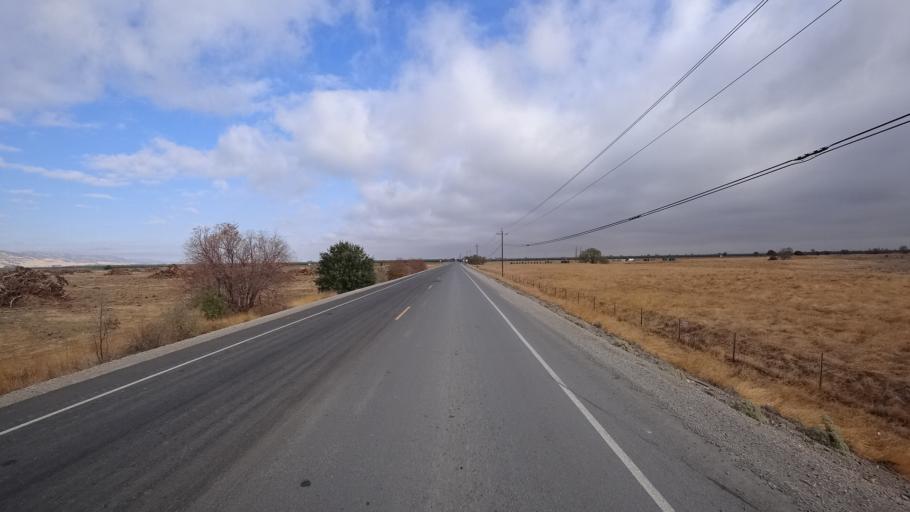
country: US
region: California
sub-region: Yolo County
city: Esparto
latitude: 38.7153
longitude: -122.0102
